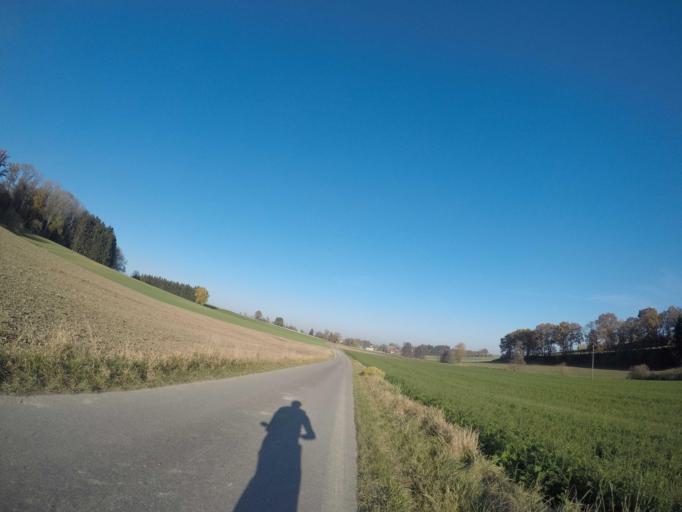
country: DE
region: Baden-Wuerttemberg
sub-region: Tuebingen Region
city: Oberstadion
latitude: 48.1842
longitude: 9.6717
